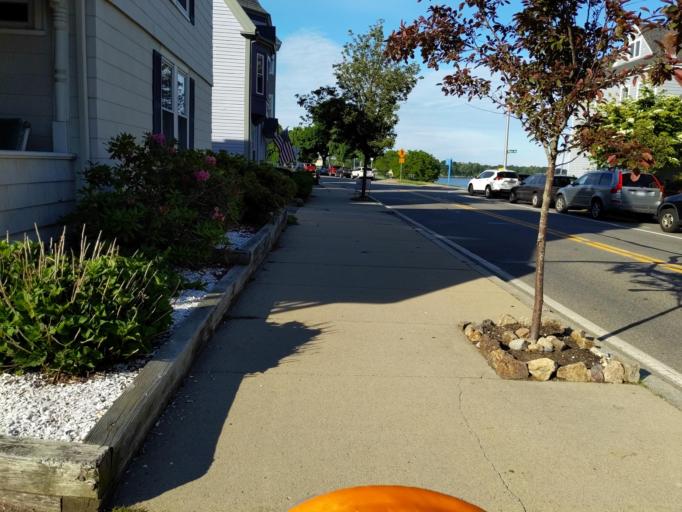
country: US
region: Massachusetts
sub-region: Essex County
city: Beverly
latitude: 42.5420
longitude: -70.8780
